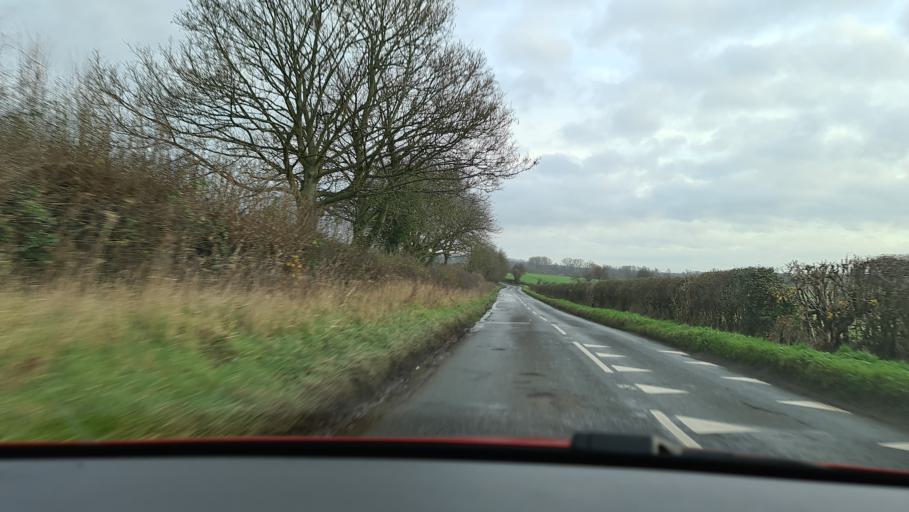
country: GB
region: England
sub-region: Buckinghamshire
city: Haddenham
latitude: 51.7915
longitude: -0.9579
